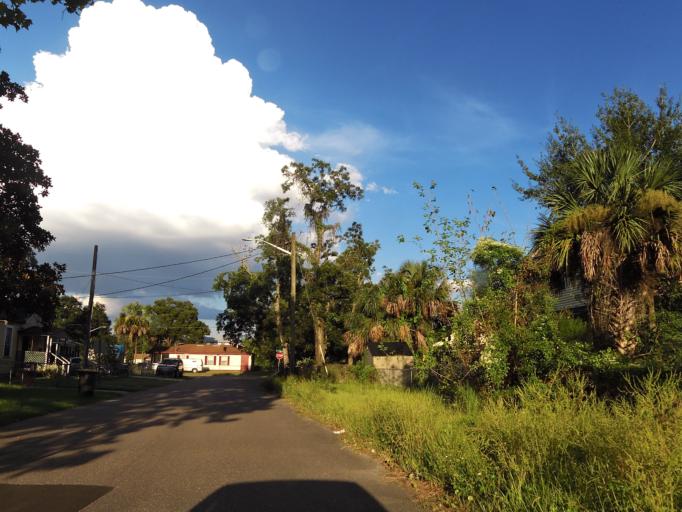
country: US
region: Florida
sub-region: Duval County
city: Jacksonville
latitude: 30.3417
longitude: -81.6862
